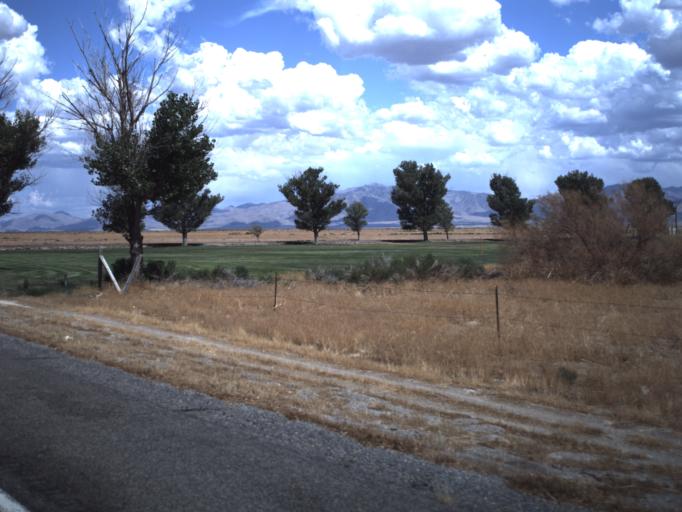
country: US
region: Utah
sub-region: Millard County
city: Delta
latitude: 39.3812
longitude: -112.5251
